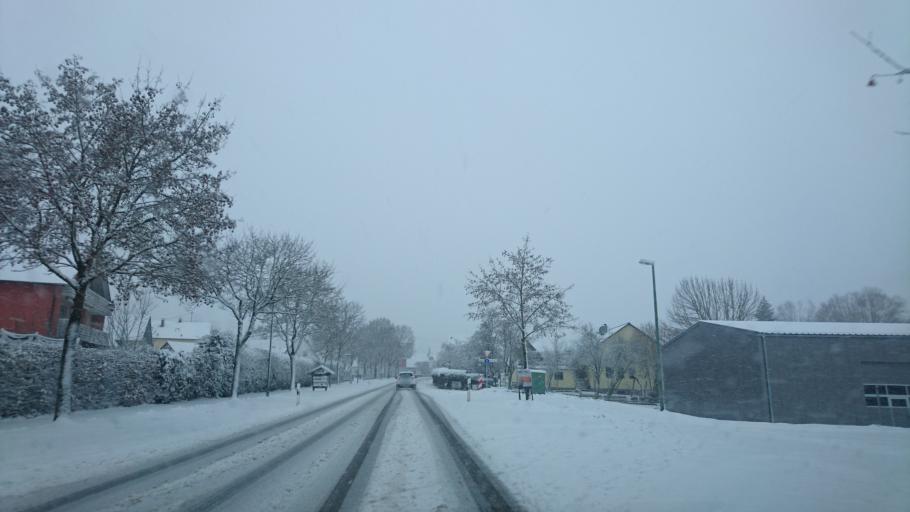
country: DE
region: Bavaria
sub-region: Swabia
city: Emersacker
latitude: 48.4949
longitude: 10.6751
